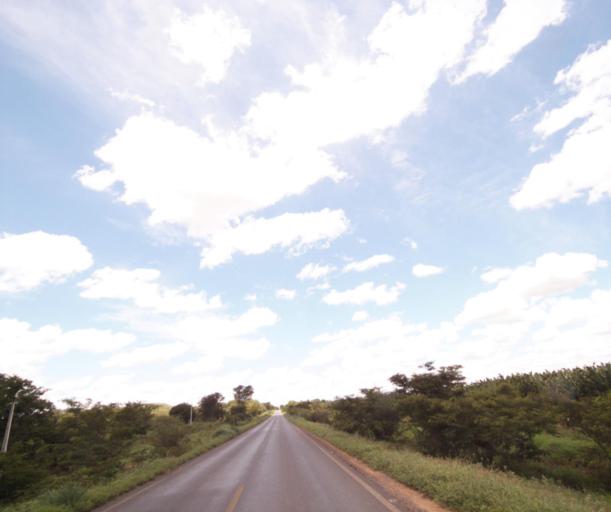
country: BR
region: Bahia
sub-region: Bom Jesus Da Lapa
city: Bom Jesus da Lapa
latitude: -13.2624
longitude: -43.5372
